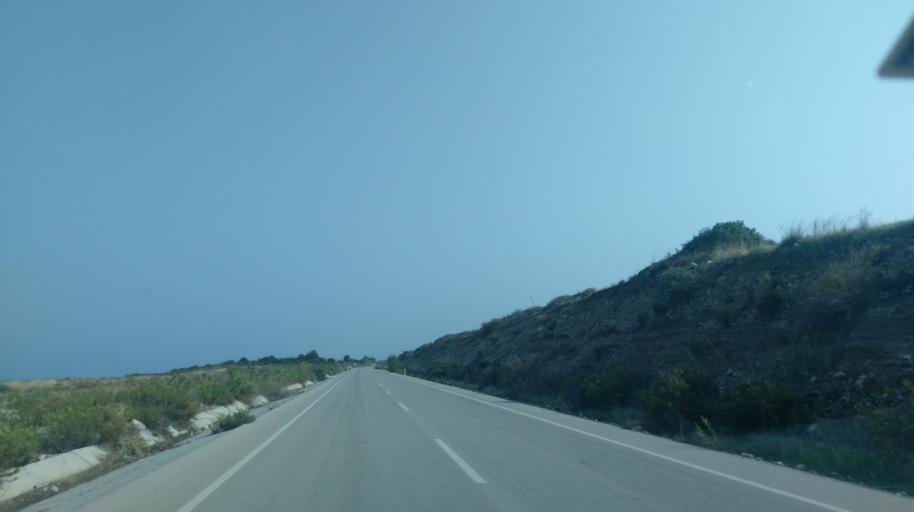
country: CY
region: Ammochostos
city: Trikomo
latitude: 35.4122
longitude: 33.8568
